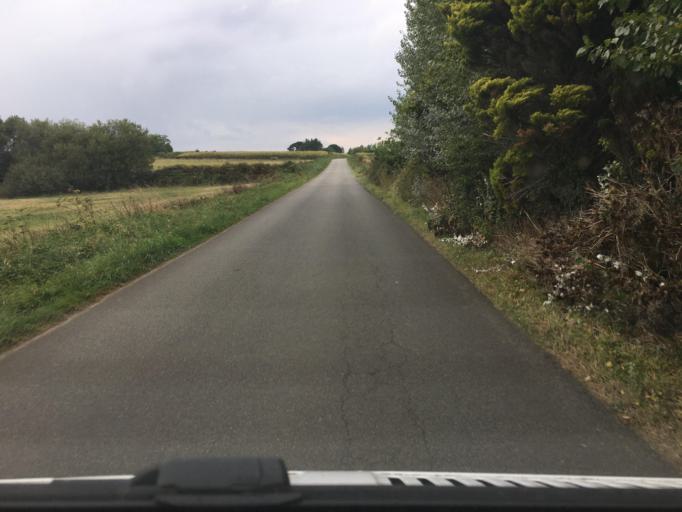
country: FR
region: Brittany
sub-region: Departement du Finistere
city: Beuzec-Cap-Sizun
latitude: 48.0747
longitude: -4.4754
